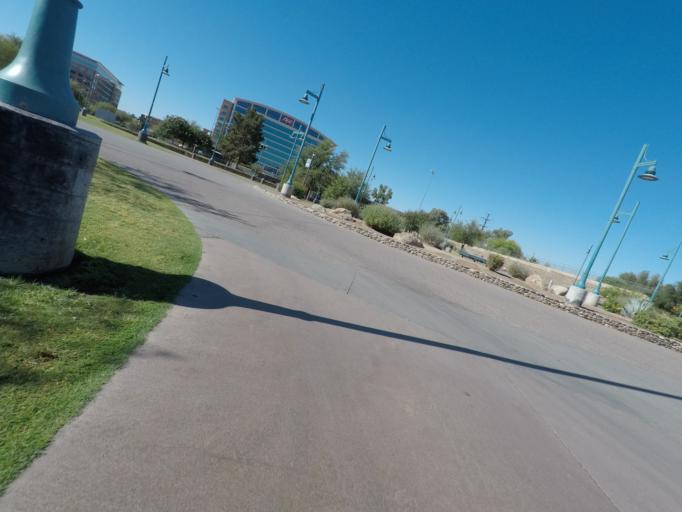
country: US
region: Arizona
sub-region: Maricopa County
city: Tempe Junction
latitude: 33.4312
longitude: -111.9415
